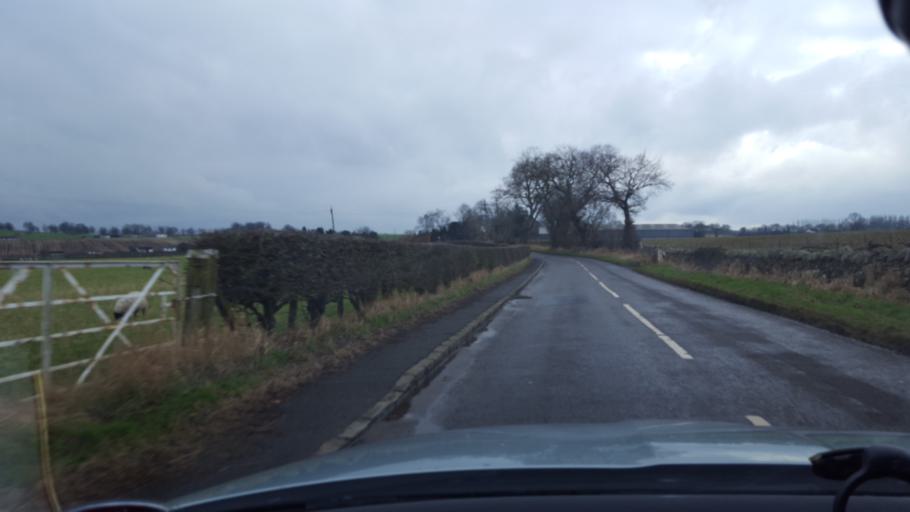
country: GB
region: Scotland
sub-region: Fife
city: Crossford
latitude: 56.0021
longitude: -3.5271
